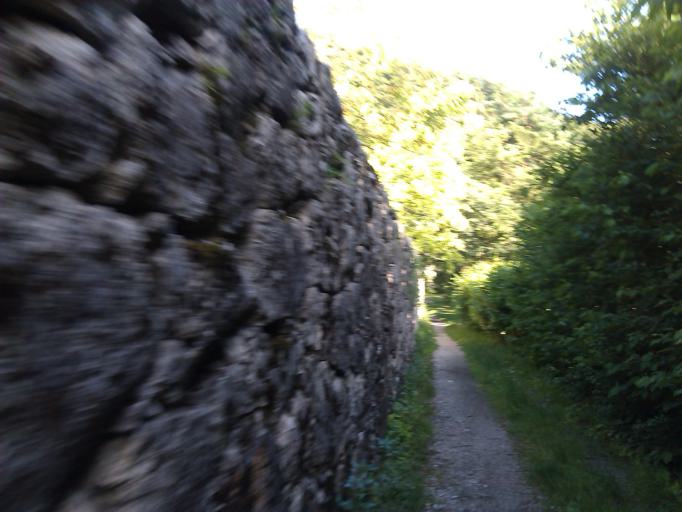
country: IT
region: Trentino-Alto Adige
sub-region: Provincia di Trento
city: Meano
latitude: 46.0991
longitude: 11.1206
